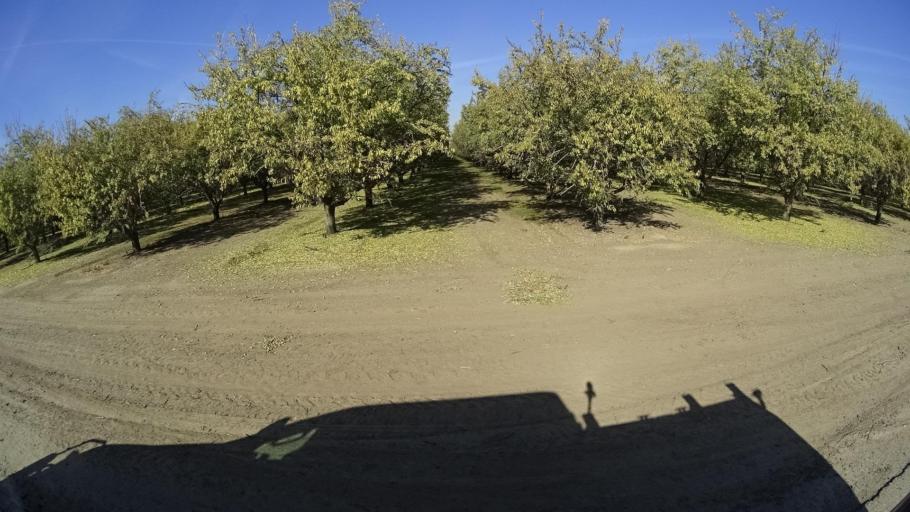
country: US
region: California
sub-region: Kern County
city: Wasco
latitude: 35.6669
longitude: -119.3652
